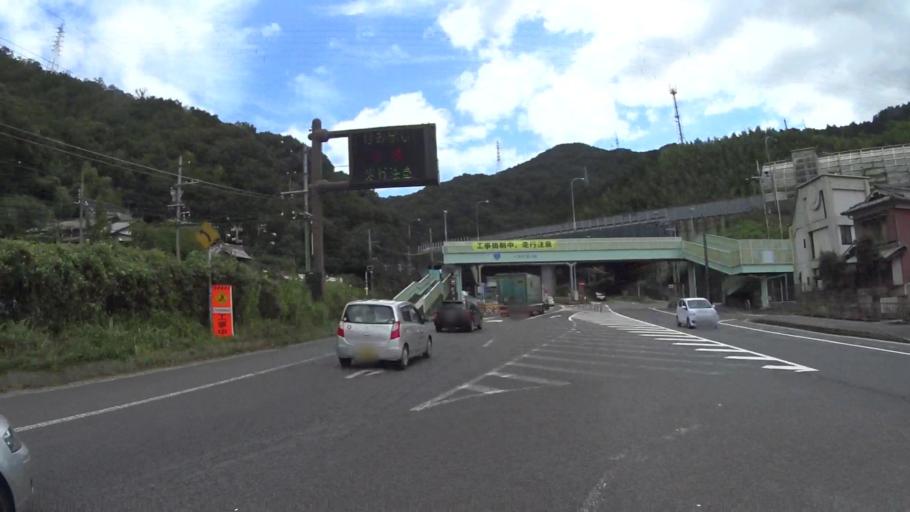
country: JP
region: Shiga Prefecture
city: Otsu-shi
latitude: 34.9907
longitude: 135.8395
